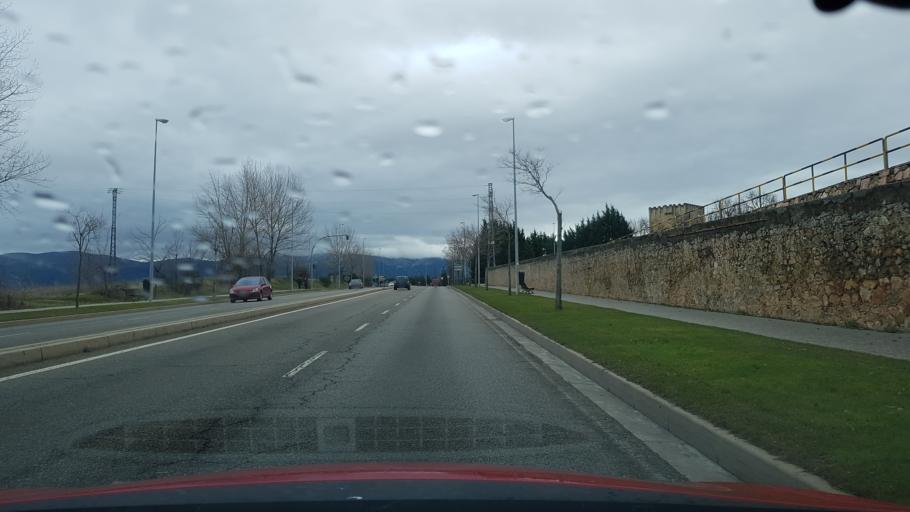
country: ES
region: Castille and Leon
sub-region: Provincia de Segovia
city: Segovia
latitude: 40.9379
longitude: -4.1013
